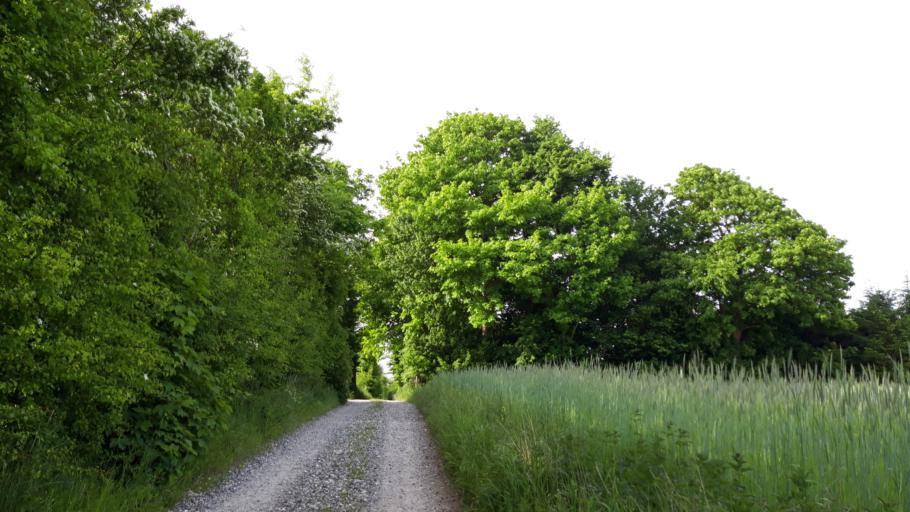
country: DK
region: Central Jutland
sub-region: Arhus Kommune
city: Lystrup
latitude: 56.2299
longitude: 10.1966
